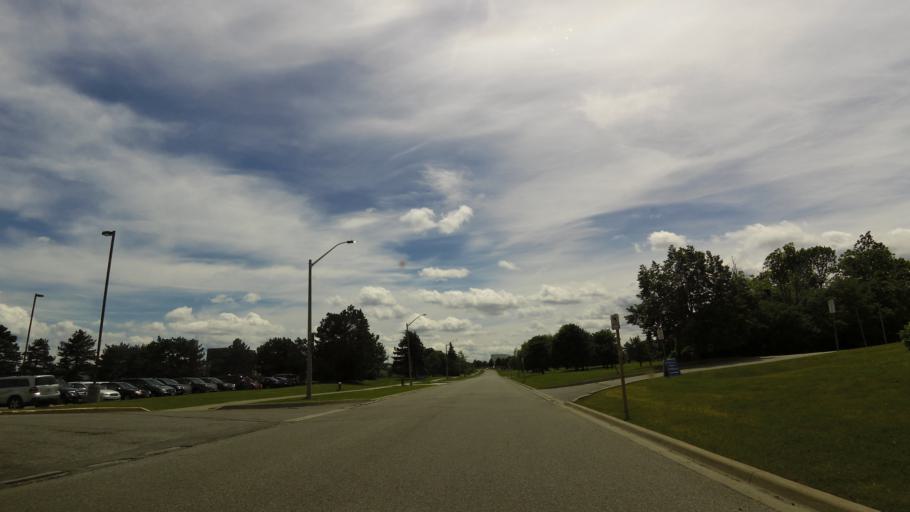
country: CA
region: Ontario
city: Mississauga
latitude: 43.5206
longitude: -79.6583
